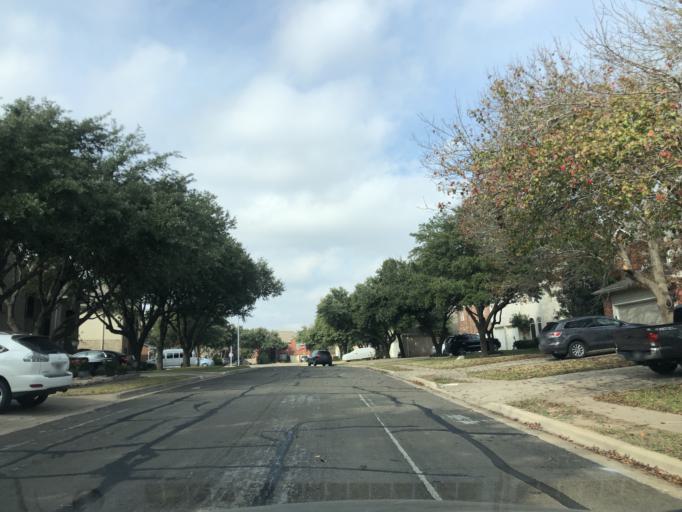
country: US
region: Texas
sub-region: Travis County
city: Wells Branch
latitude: 30.4204
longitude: -97.6810
